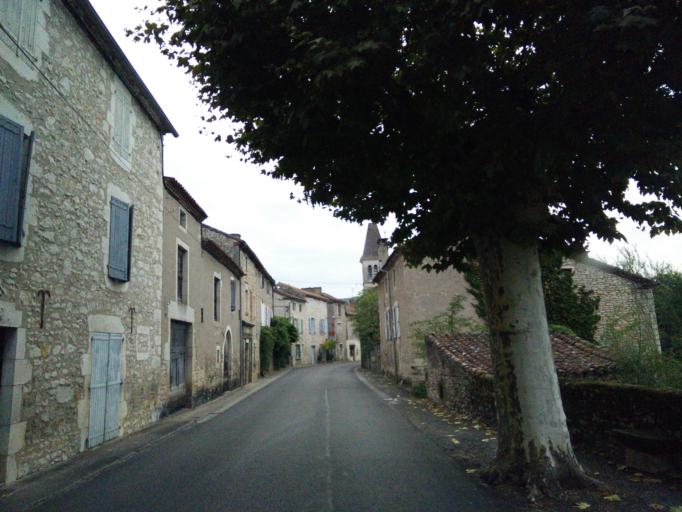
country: FR
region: Midi-Pyrenees
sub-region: Departement du Lot
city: Lalbenque
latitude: 44.4784
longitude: 1.5770
